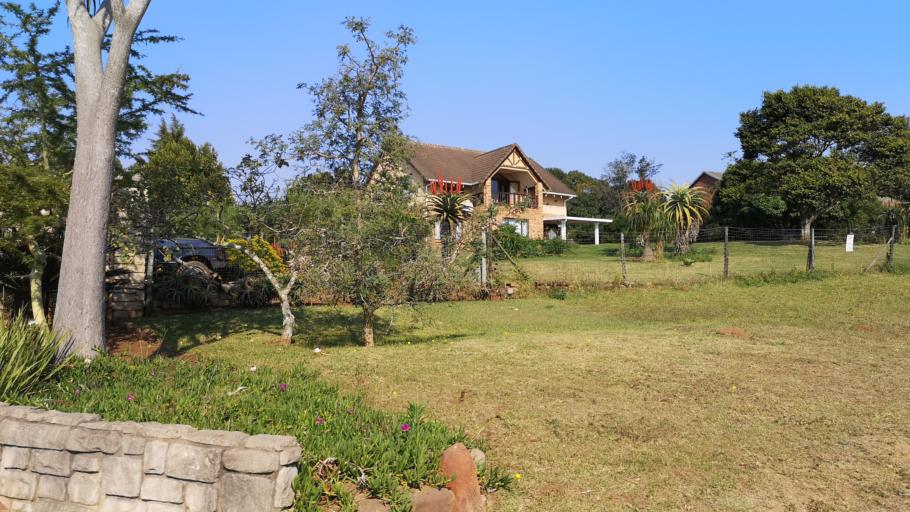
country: ZA
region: KwaZulu-Natal
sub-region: eThekwini Metropolitan Municipality
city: Mpumalanga
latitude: -29.7357
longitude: 30.6838
